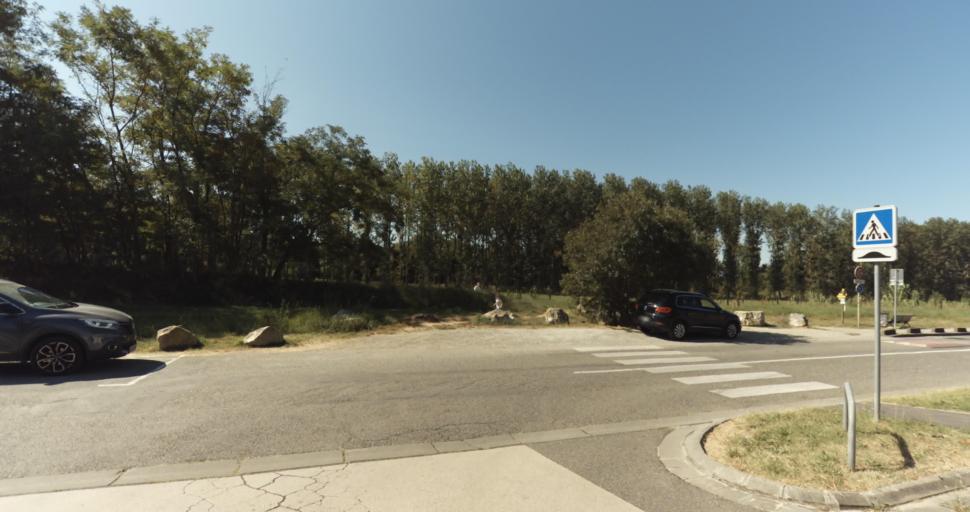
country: FR
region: Midi-Pyrenees
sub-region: Departement de la Haute-Garonne
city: Saint-Jean
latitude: 43.6477
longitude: 1.4997
